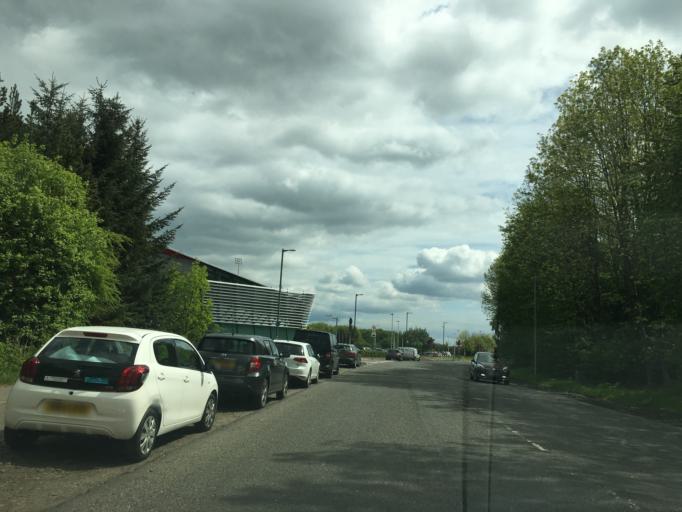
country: GB
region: Scotland
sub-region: Stirling
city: Stirling
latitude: 56.1180
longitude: -3.9160
